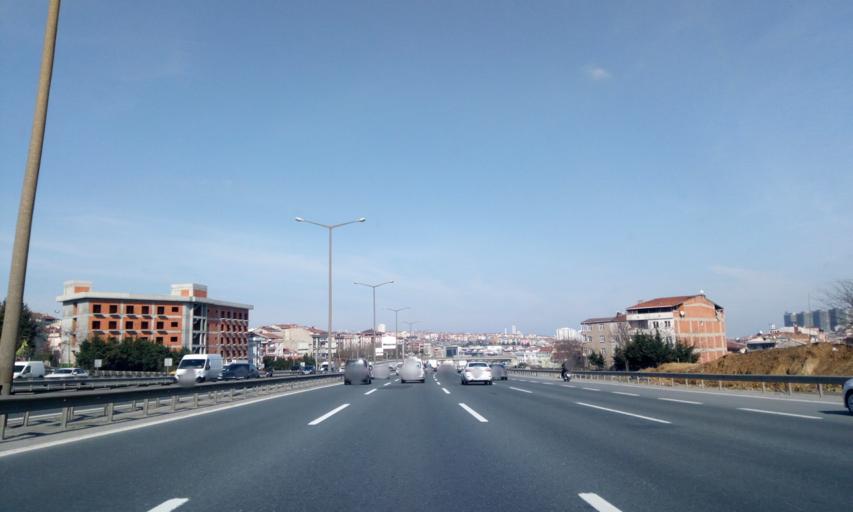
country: TR
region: Istanbul
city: Sultangazi
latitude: 41.0832
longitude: 28.8761
